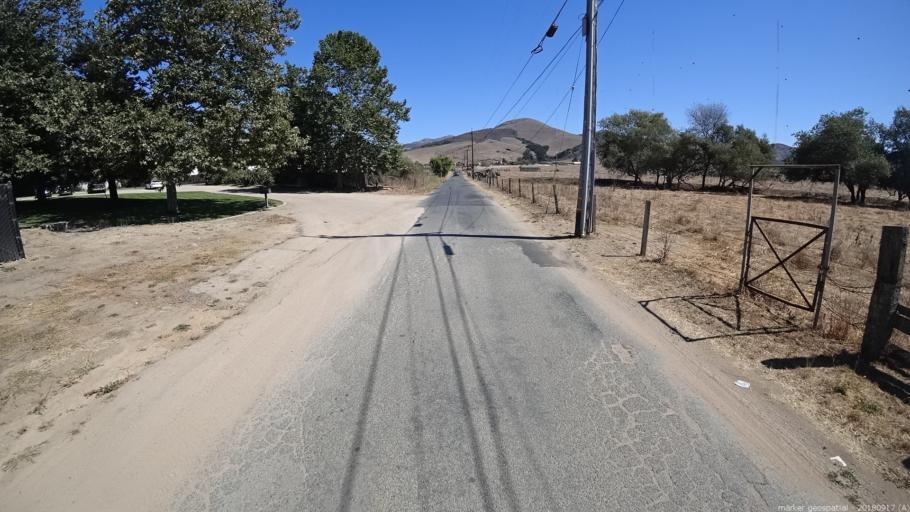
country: US
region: California
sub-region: Monterey County
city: Salinas
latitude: 36.7329
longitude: -121.5961
